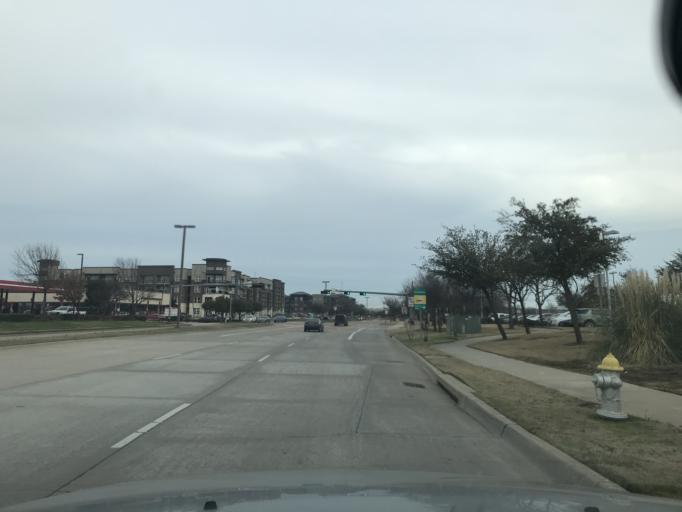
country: US
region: Texas
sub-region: Dallas County
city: Carrollton
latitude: 32.9939
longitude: -96.9391
